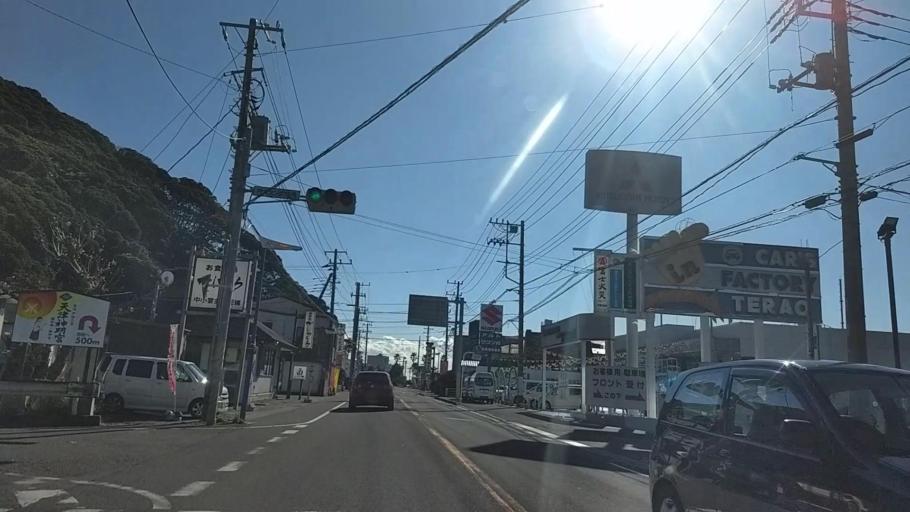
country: JP
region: Chiba
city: Kawaguchi
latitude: 35.1231
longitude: 140.1725
